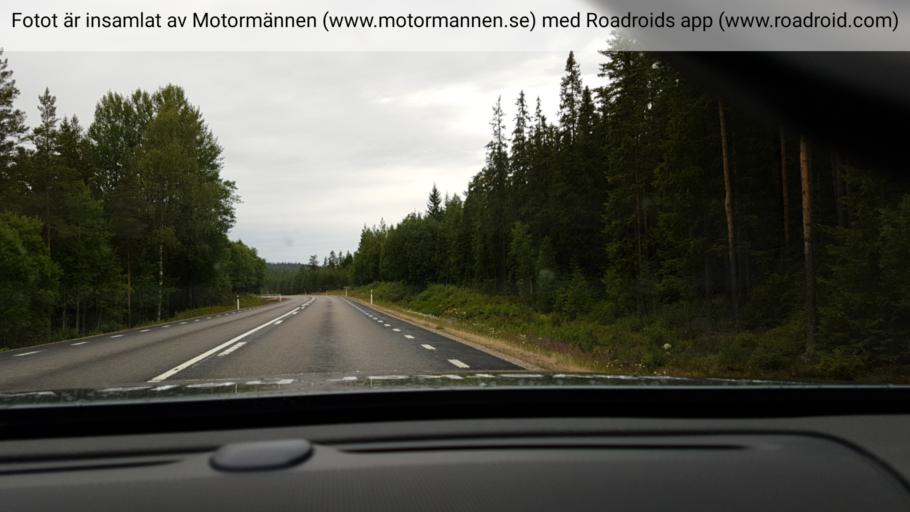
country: SE
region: Dalarna
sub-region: Rattviks Kommun
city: Raettvik
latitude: 60.7971
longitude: 15.2717
